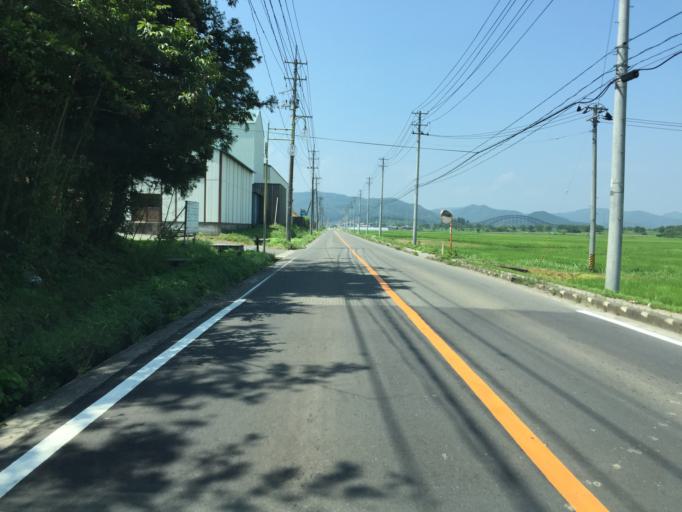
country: JP
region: Miyagi
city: Marumori
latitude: 37.9097
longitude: 140.7858
